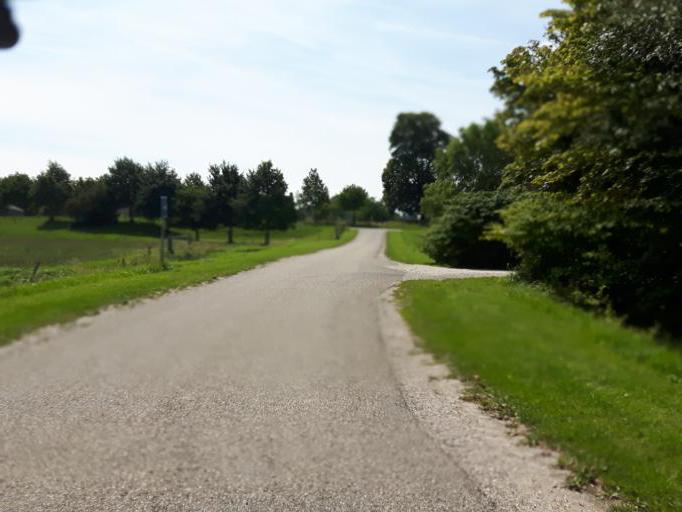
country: NL
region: Zeeland
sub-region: Gemeente Goes
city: Goes
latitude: 51.4733
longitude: 3.8362
